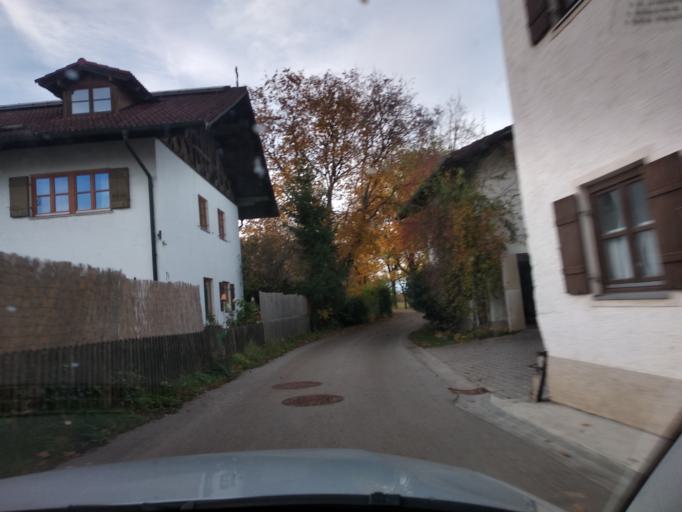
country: DE
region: Bavaria
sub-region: Upper Bavaria
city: Grafing bei Munchen
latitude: 48.0348
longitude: 11.9894
